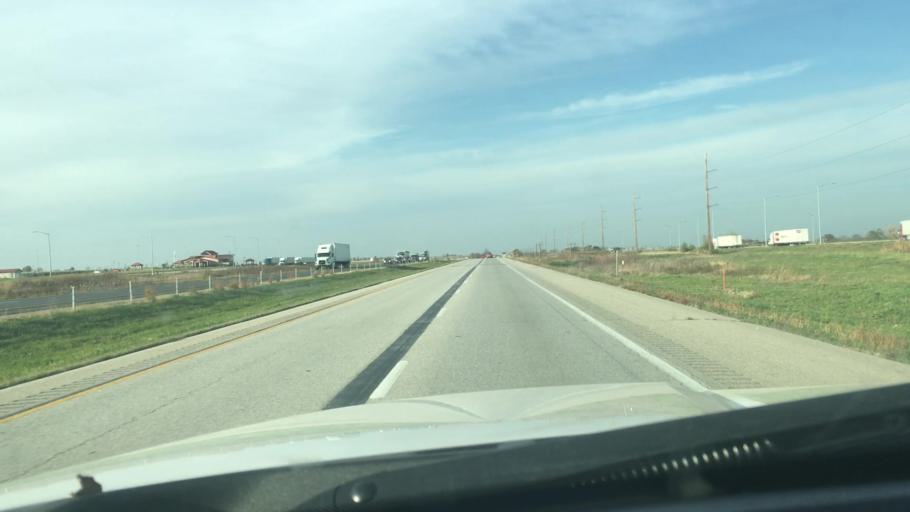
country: US
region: Iowa
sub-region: Story County
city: Huxley
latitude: 41.8284
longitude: -93.5709
